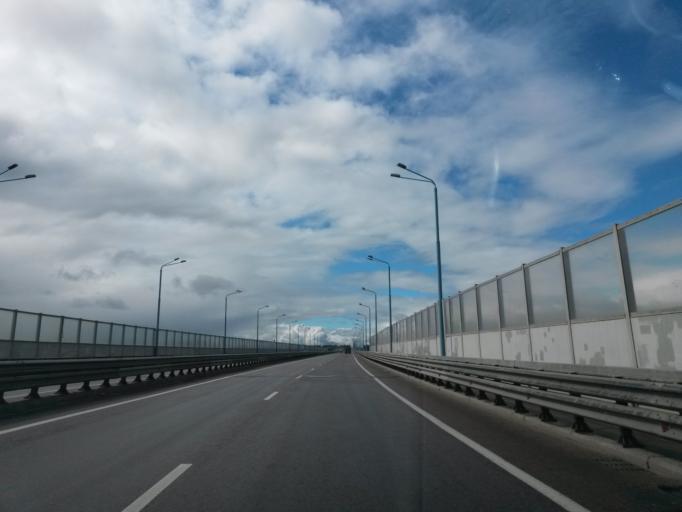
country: RU
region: Jaroslavl
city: Yaroslavl
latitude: 57.6791
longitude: 39.8682
